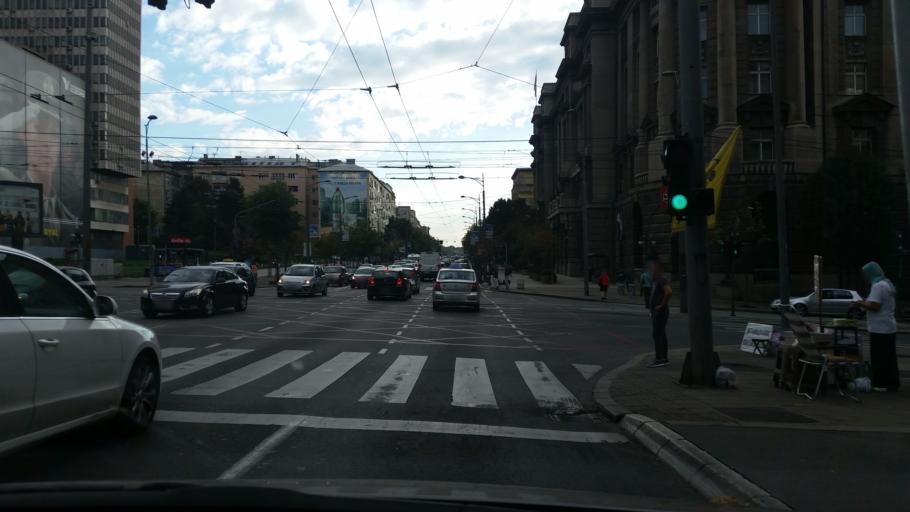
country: RS
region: Central Serbia
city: Belgrade
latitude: 44.8060
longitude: 20.4605
